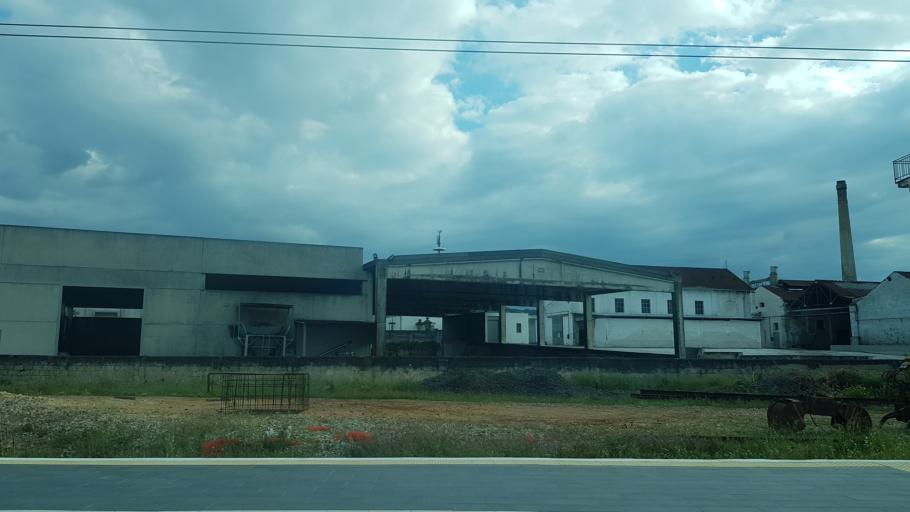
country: IT
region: Apulia
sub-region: Provincia di Brindisi
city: Ostuni
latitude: 40.7528
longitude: 17.5789
